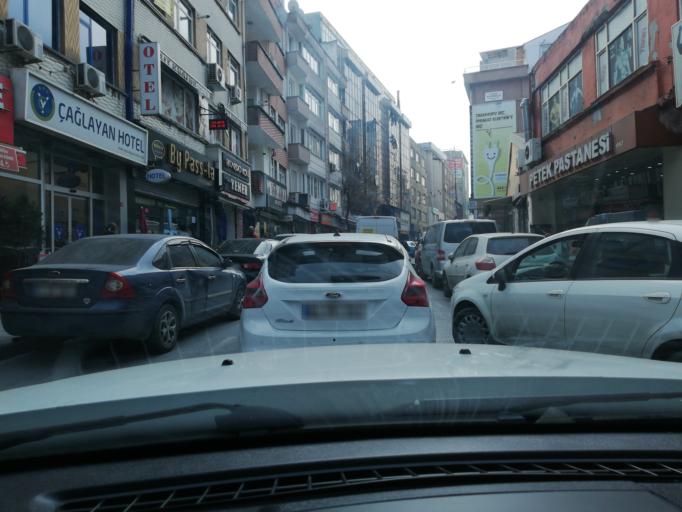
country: TR
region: Istanbul
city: Sisli
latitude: 41.0741
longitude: 28.9809
